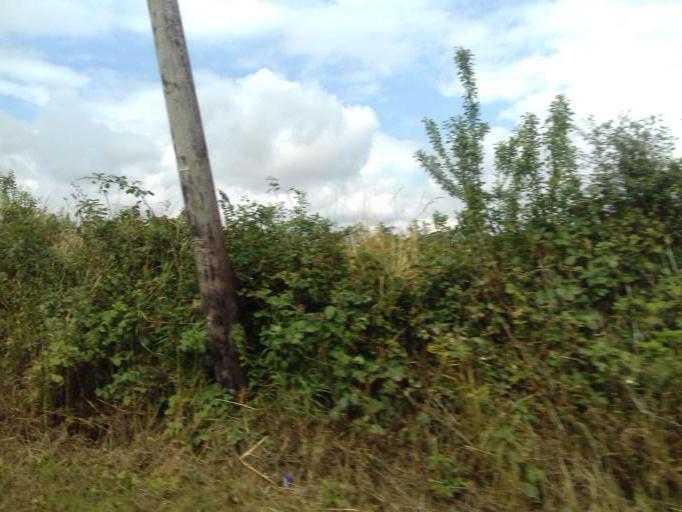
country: IE
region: Leinster
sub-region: Loch Garman
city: Ballinroad
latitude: 52.4754
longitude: -6.4088
